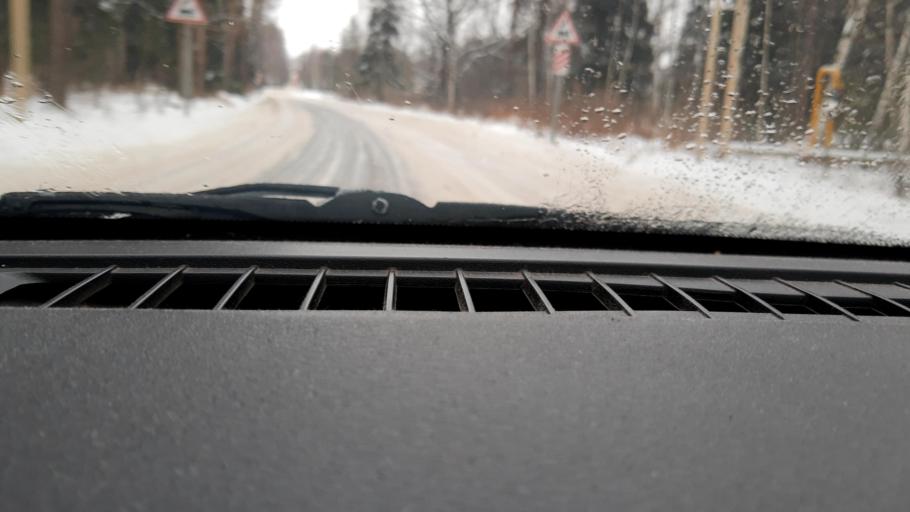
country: RU
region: Nizjnij Novgorod
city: Afonino
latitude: 56.1867
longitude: 44.0796
